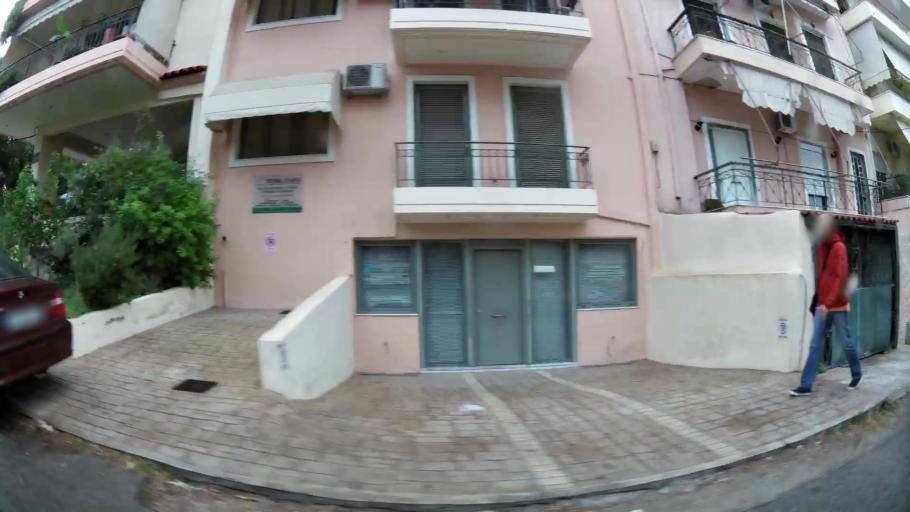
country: GR
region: Attica
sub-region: Nomarchia Athinas
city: Agia Varvara
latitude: 37.9882
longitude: 23.6545
